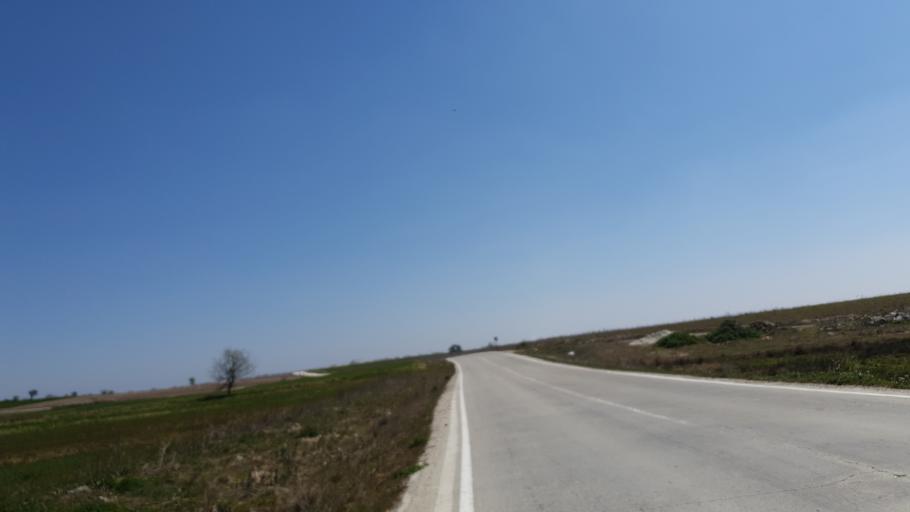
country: TR
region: Tekirdag
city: Cerkezkoey
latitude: 41.3236
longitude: 27.9320
